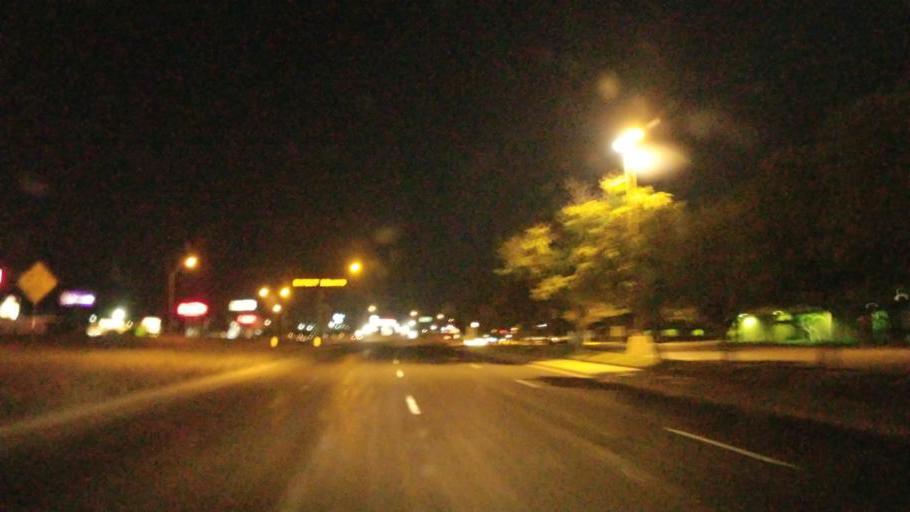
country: US
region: Texas
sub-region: Potter County
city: Amarillo
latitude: 35.1875
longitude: -101.9148
